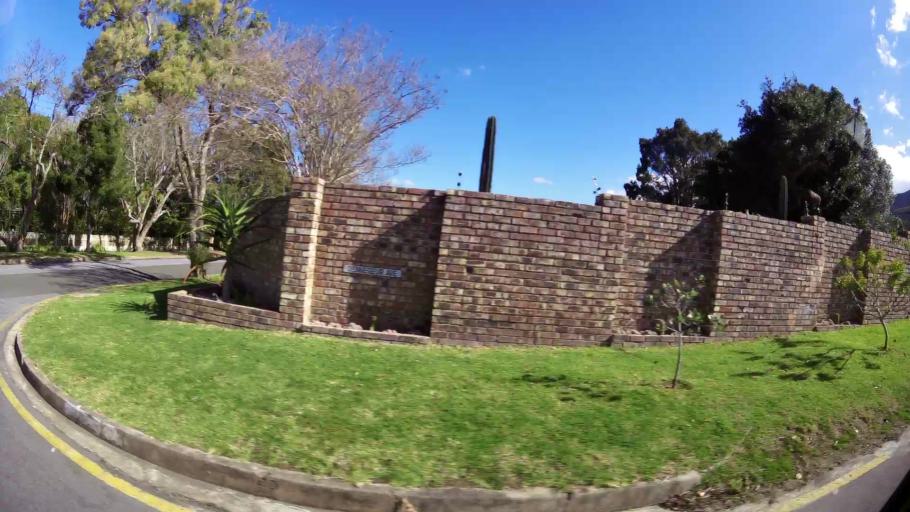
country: ZA
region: Western Cape
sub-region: Eden District Municipality
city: George
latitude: -33.9398
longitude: 22.4737
